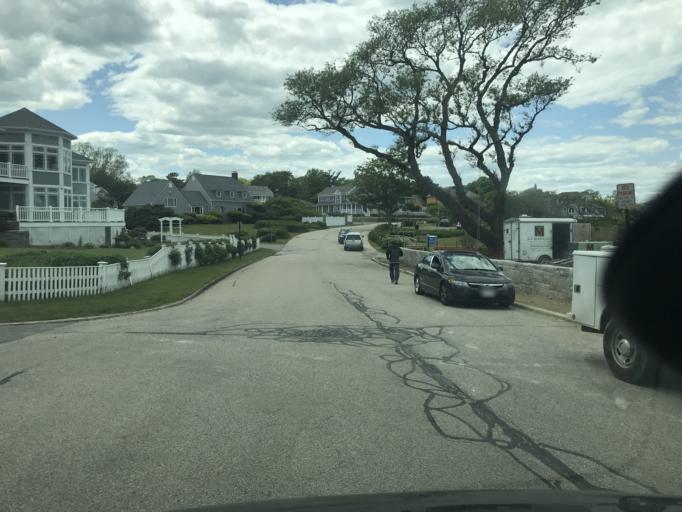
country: US
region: Massachusetts
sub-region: Essex County
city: Rockport
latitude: 42.6580
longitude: -70.6071
